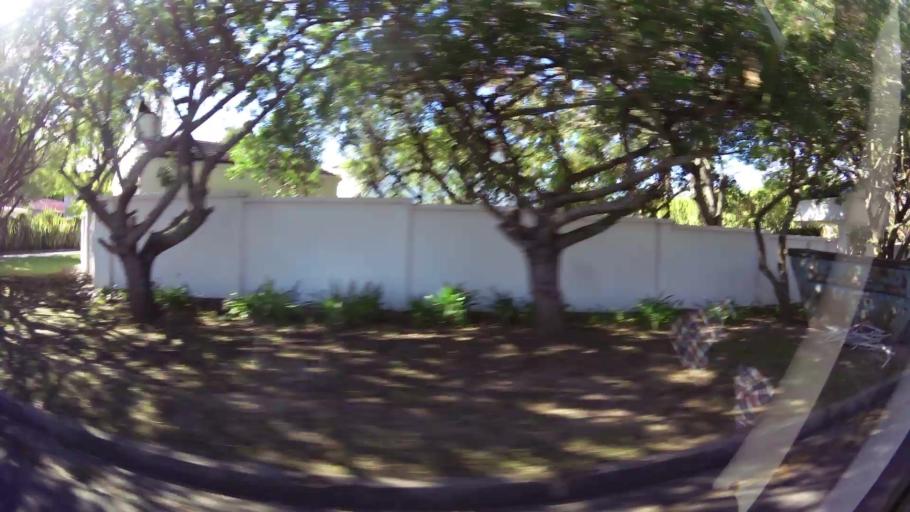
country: ZA
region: Western Cape
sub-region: Eden District Municipality
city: George
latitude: -33.9513
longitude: 22.4441
